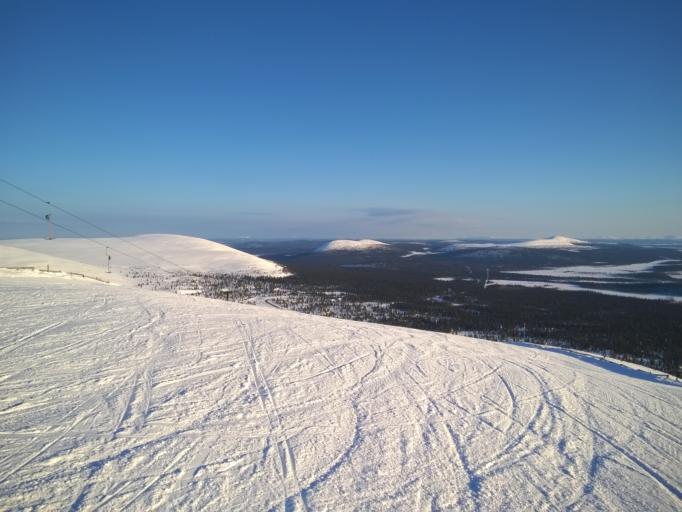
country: FI
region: Lapland
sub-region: Tunturi-Lappi
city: Muonio
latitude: 68.0548
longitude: 24.0397
